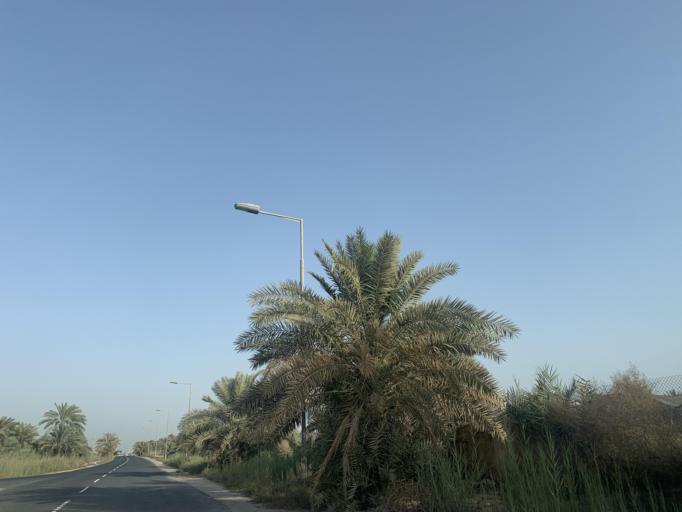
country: BH
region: Central Governorate
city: Madinat Hamad
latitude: 26.1790
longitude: 50.4551
